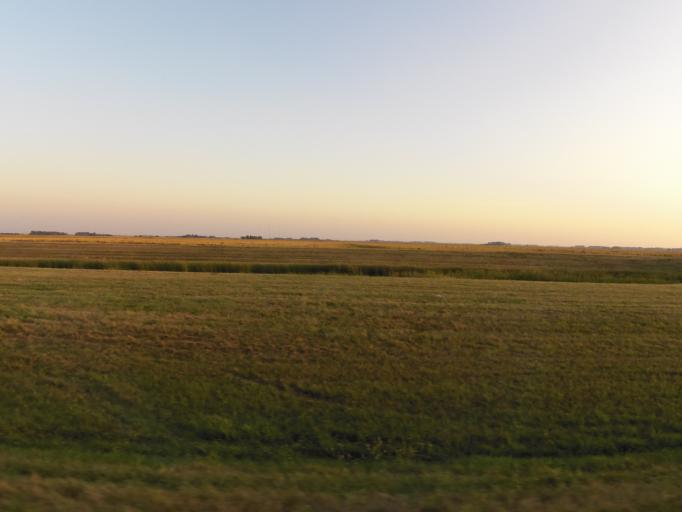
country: US
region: North Dakota
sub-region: Grand Forks County
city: Grand Forks
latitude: 47.8603
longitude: -97.0277
